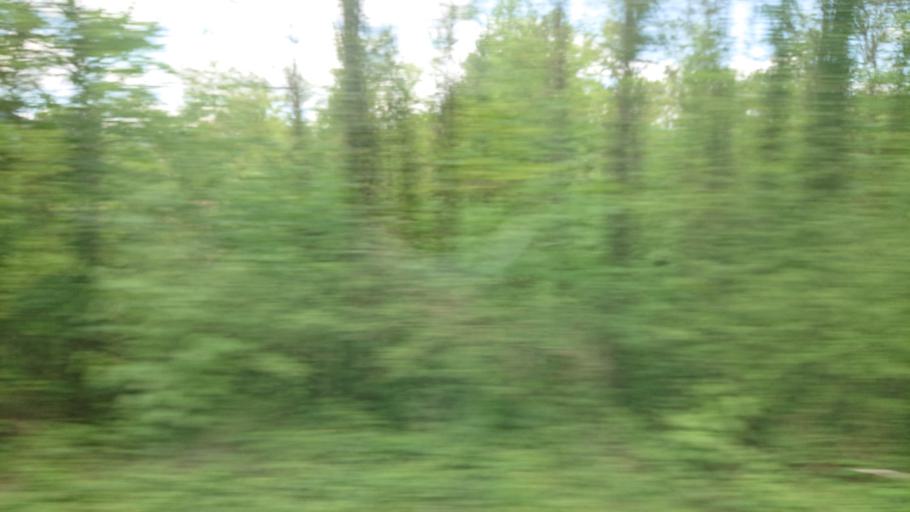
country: FR
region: Rhone-Alpes
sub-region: Departement de l'Ain
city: Artemare
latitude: 45.8624
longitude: 5.6960
